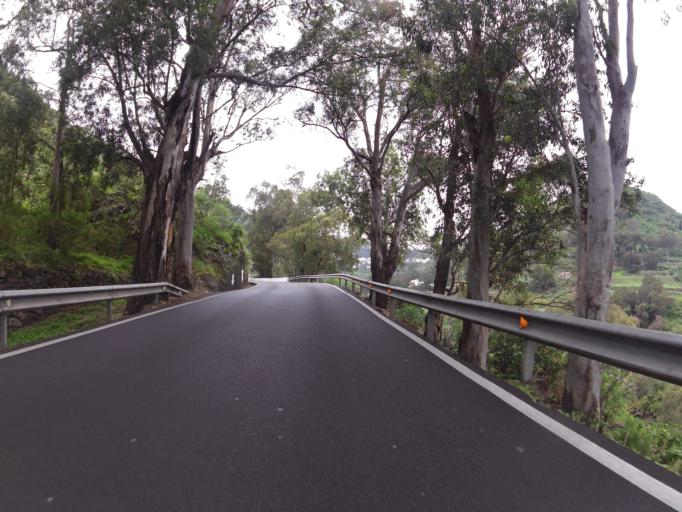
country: ES
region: Canary Islands
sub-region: Provincia de Las Palmas
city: Teror
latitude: 28.0737
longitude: -15.5238
